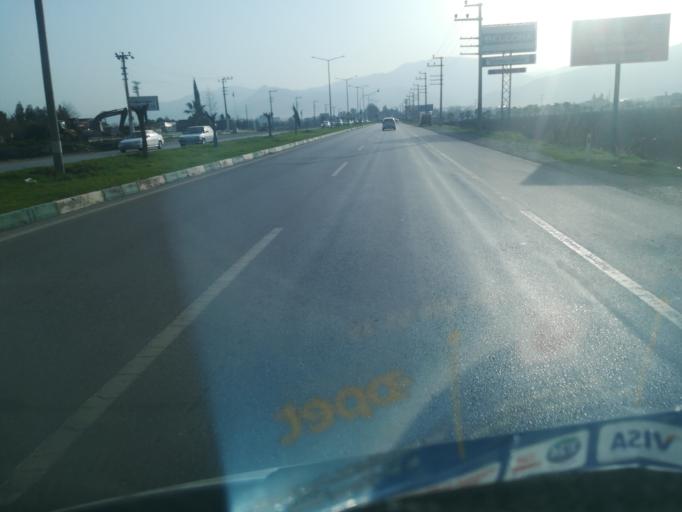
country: TR
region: Osmaniye
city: Toprakkale
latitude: 37.0560
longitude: 36.1977
